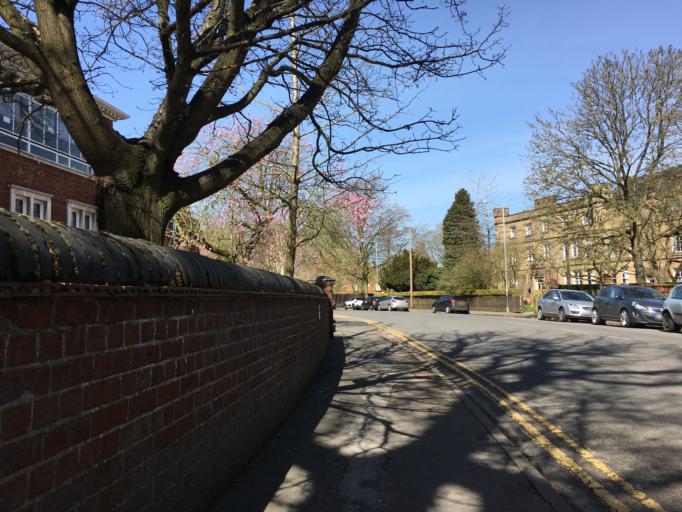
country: GB
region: England
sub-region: Warwickshire
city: Rugby
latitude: 52.3673
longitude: -1.2605
